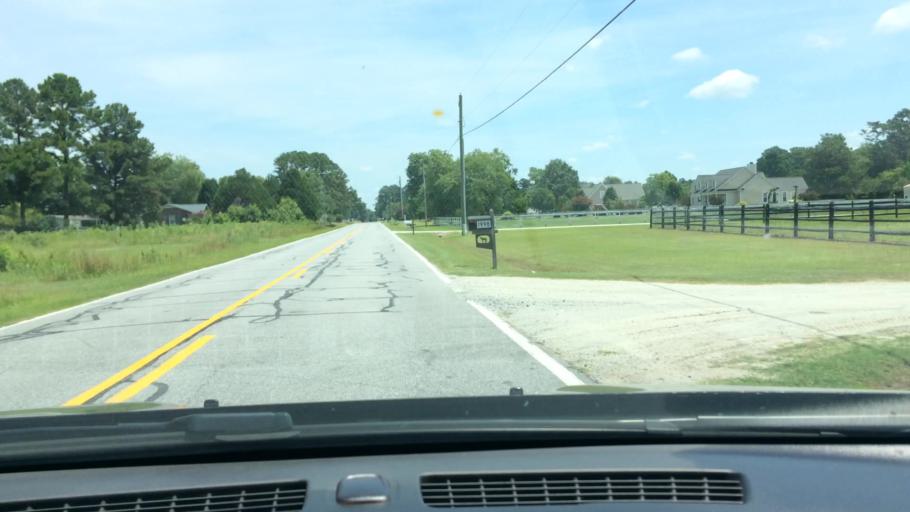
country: US
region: North Carolina
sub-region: Pitt County
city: Windsor
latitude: 35.4992
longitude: -77.3348
